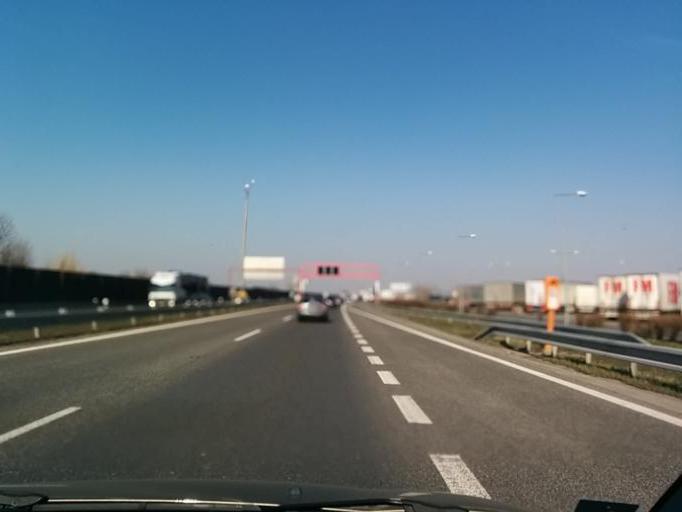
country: SK
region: Bratislavsky
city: Svaty Jur
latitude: 48.1772
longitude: 17.1906
